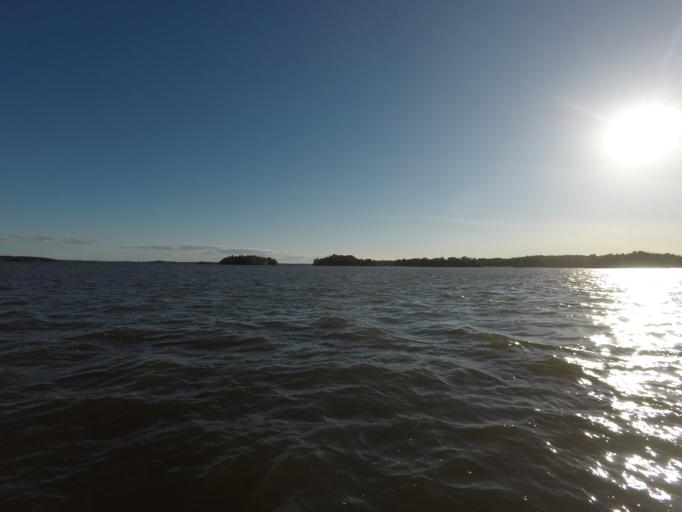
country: SE
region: Soedermanland
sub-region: Eskilstuna Kommun
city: Torshalla
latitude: 59.5024
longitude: 16.5196
